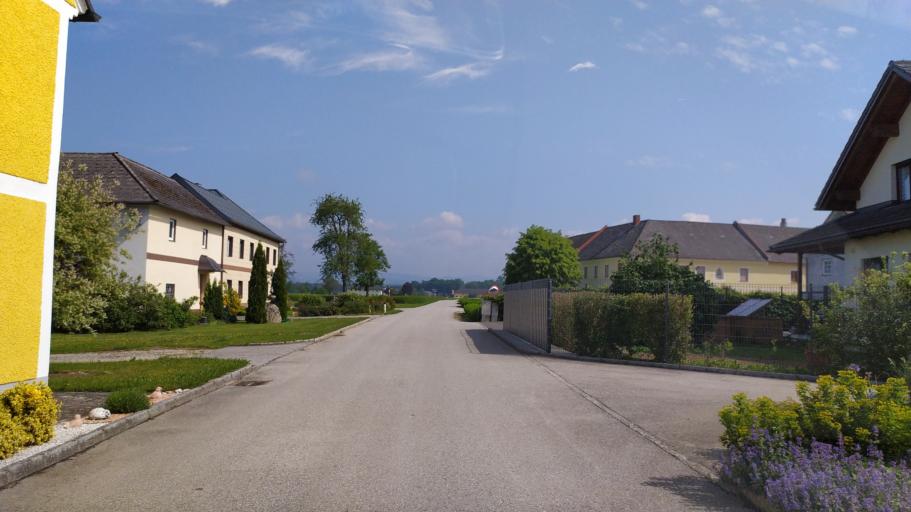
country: AT
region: Upper Austria
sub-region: Politischer Bezirk Perg
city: Perg
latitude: 48.1986
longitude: 14.6642
